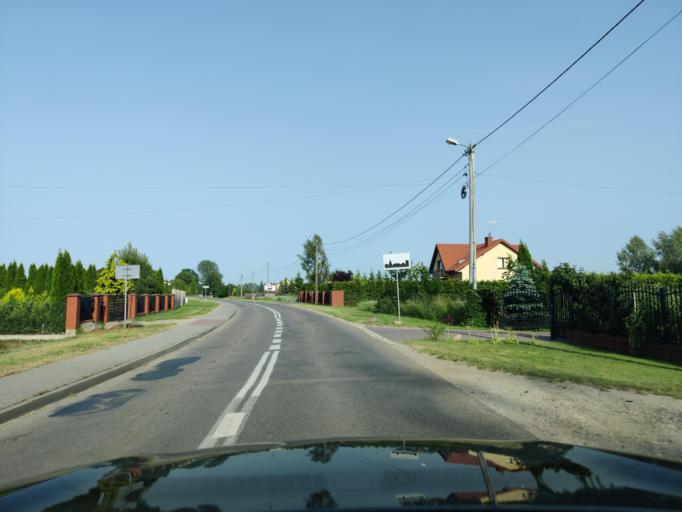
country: PL
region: Masovian Voivodeship
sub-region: Powiat wyszkowski
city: Rzasnik
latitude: 52.6990
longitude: 21.3982
